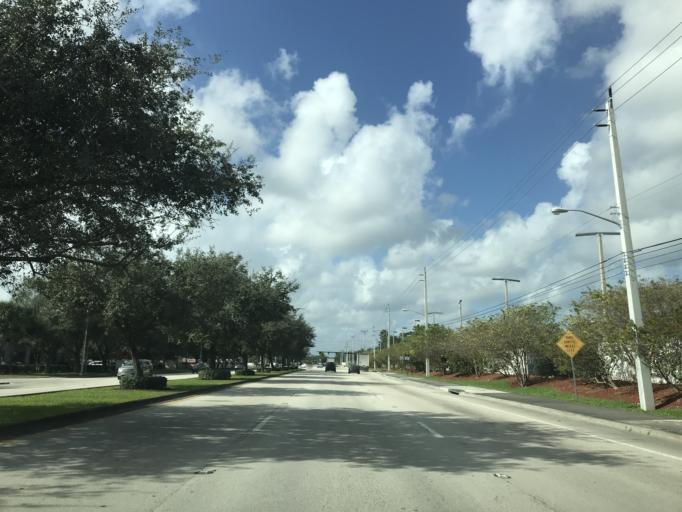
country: US
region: Florida
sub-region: Broward County
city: Coconut Creek
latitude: 26.2601
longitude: -80.1614
